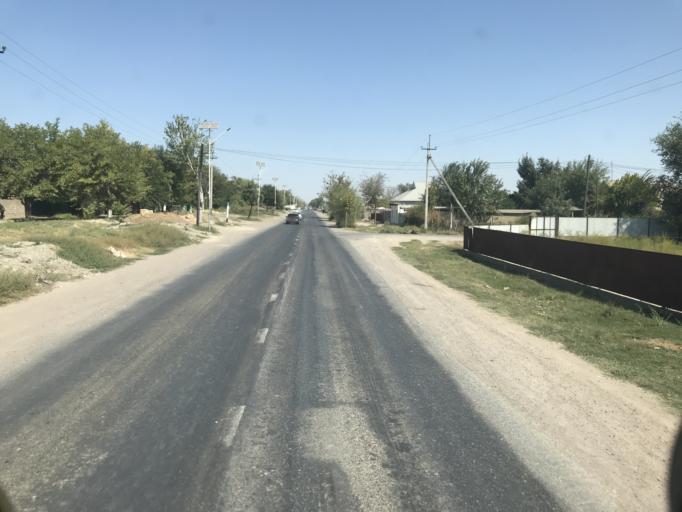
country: KZ
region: Ongtustik Qazaqstan
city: Ilyich
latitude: 40.9295
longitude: 68.4883
